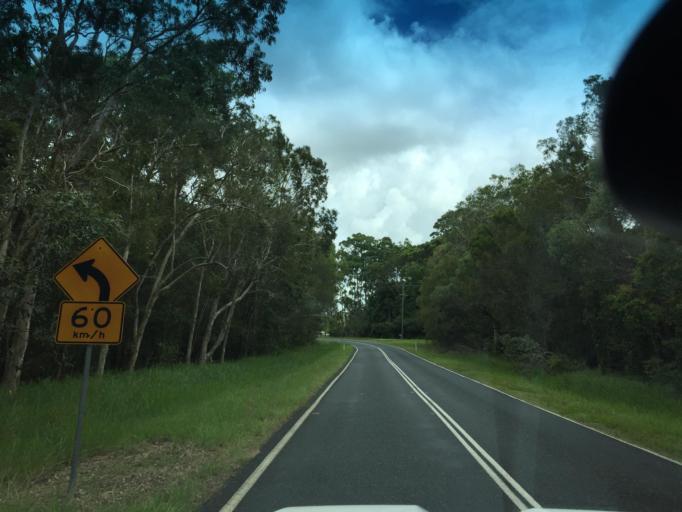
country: AU
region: Queensland
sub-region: Moreton Bay
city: Caboolture
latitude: -27.0440
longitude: 152.9162
